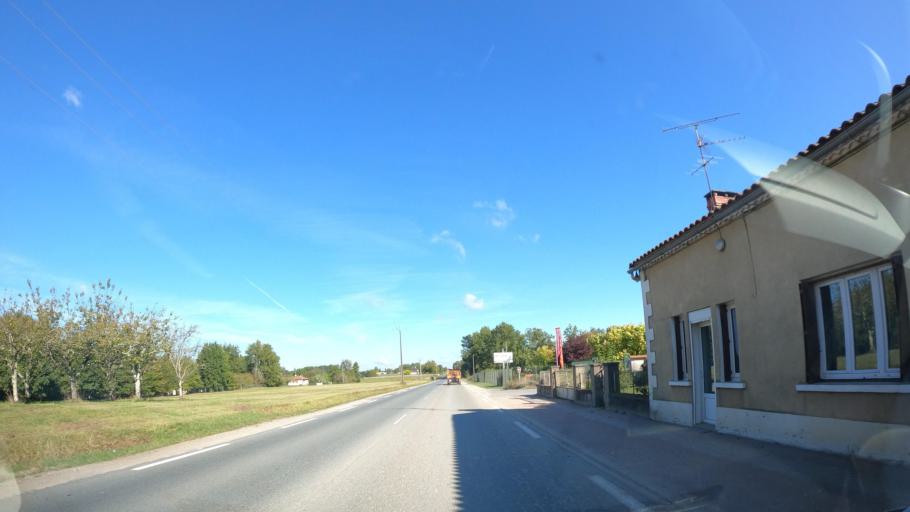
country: FR
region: Aquitaine
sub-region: Departement de la Dordogne
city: Notre-Dame-de-Sanilhac
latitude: 45.1110
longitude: 0.6931
